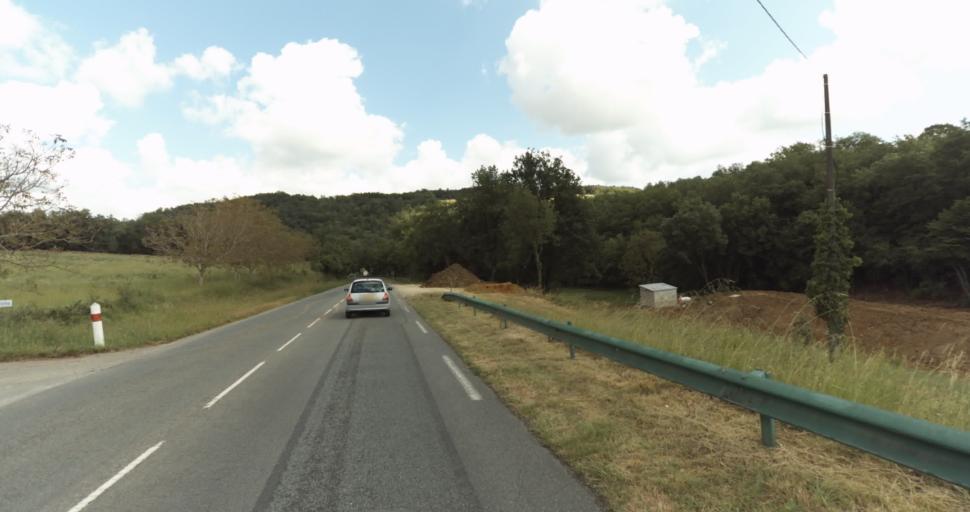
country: FR
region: Aquitaine
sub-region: Departement de la Dordogne
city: Beaumont-du-Perigord
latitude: 44.7831
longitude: 0.7661
